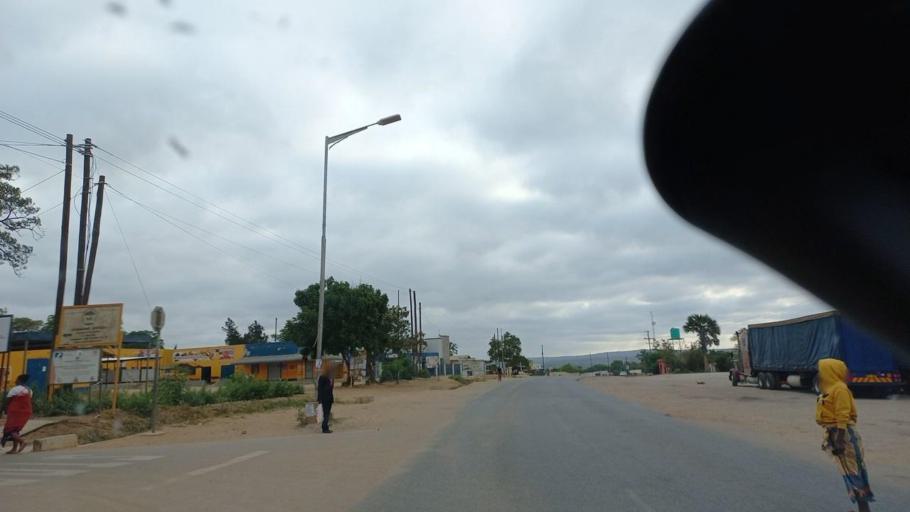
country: ZM
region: Lusaka
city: Chongwe
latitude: -15.3274
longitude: 28.6793
